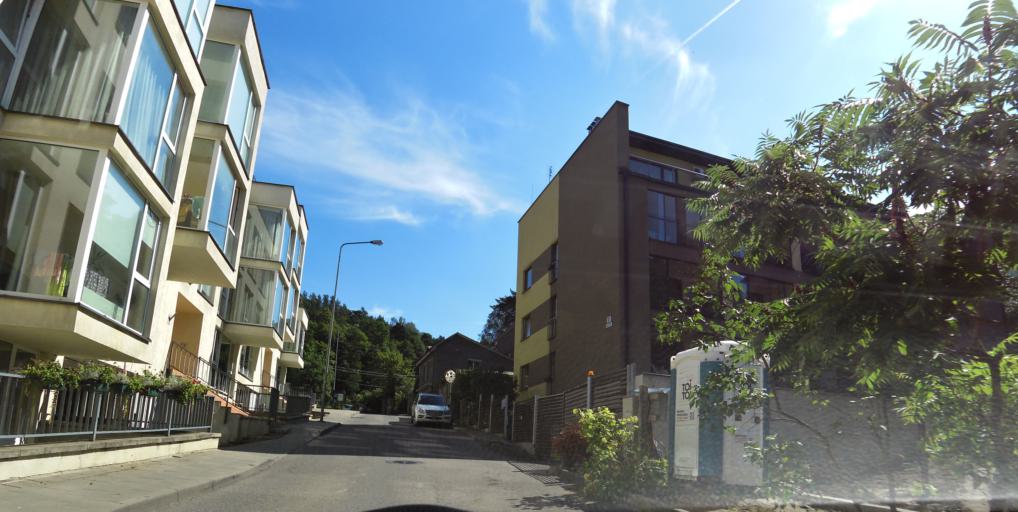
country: LT
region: Vilnius County
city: Rasos
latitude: 54.6911
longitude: 25.3139
